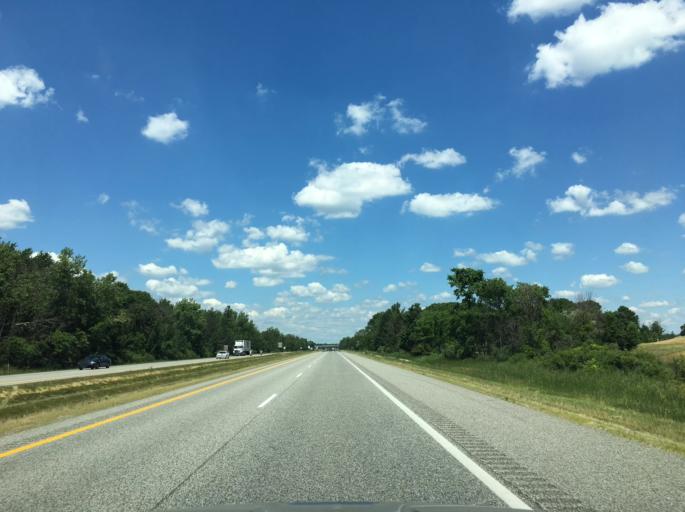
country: US
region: Michigan
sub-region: Midland County
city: Midland
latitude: 43.6309
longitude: -84.1800
